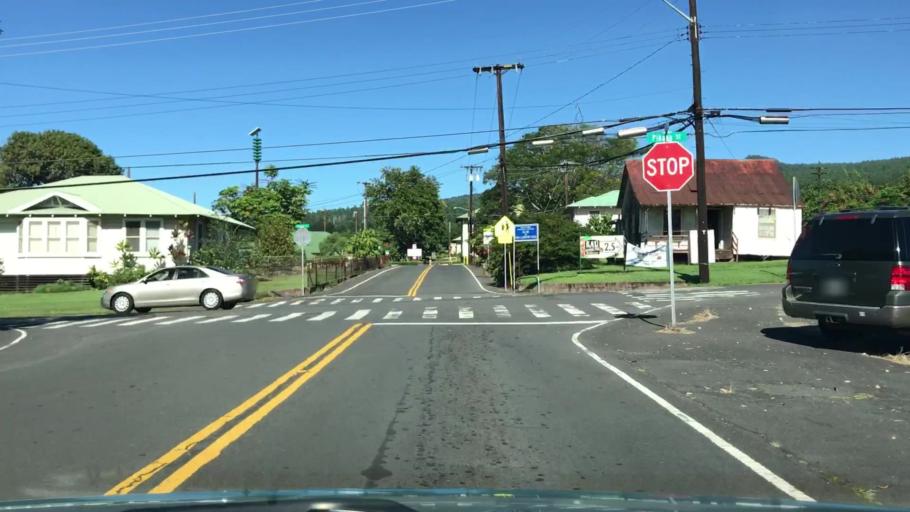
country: US
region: Hawaii
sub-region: Hawaii County
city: Pahala
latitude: 19.2025
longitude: -155.4770
